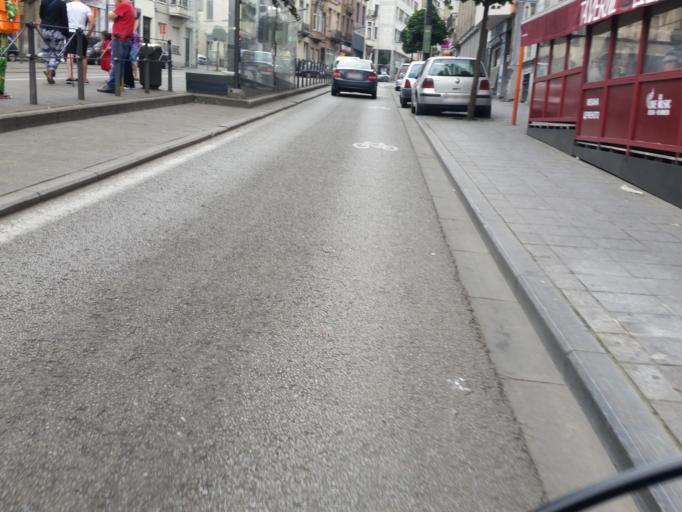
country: BE
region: Brussels Capital
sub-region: Bruxelles-Capitale
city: Brussels
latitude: 50.8633
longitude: 4.3665
